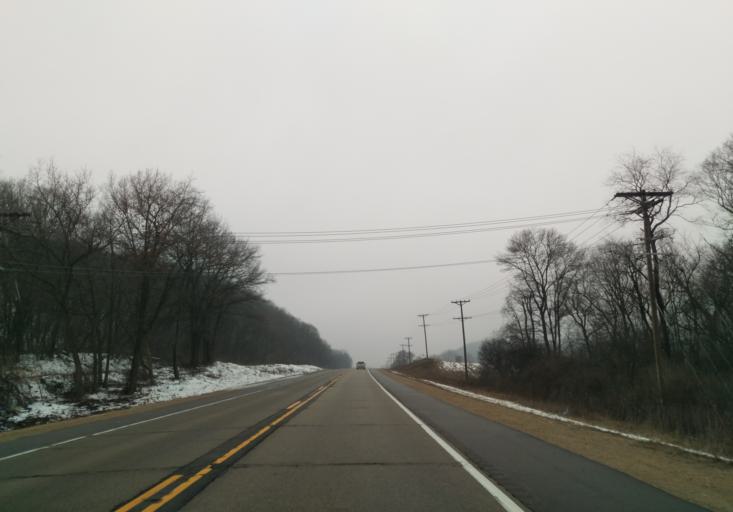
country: US
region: Wisconsin
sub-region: Dane County
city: Cross Plains
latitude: 43.0916
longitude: -89.5950
